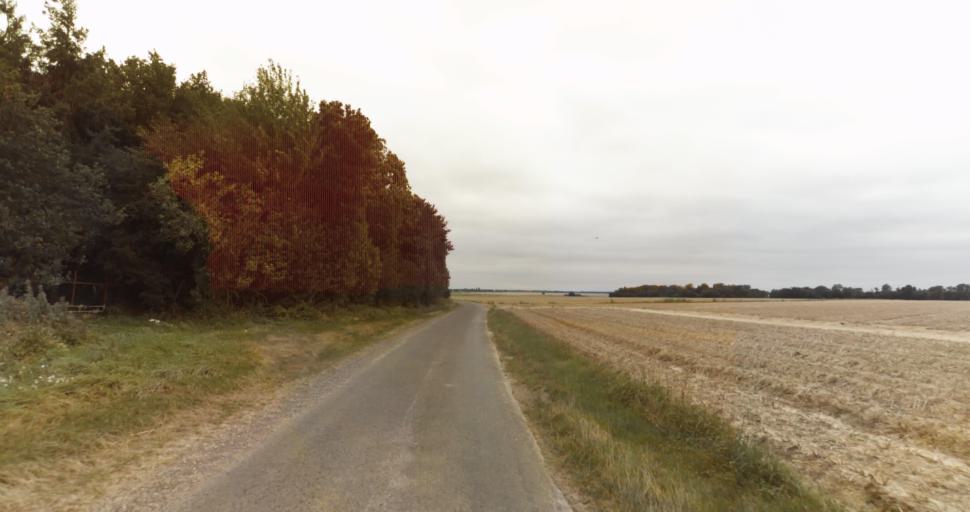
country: FR
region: Haute-Normandie
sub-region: Departement de l'Eure
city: La Couture-Boussey
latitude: 48.9249
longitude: 1.3610
